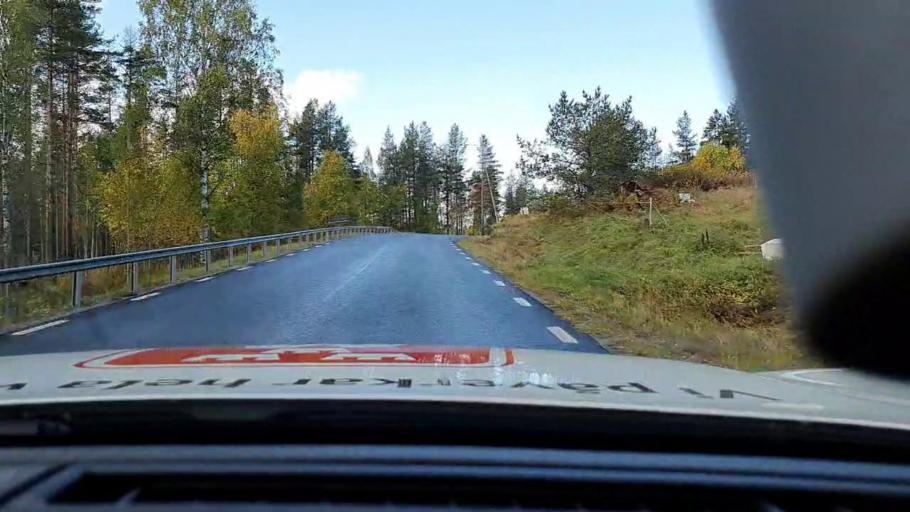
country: SE
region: Vaesterbotten
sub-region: Skelleftea Kommun
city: Langsele
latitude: 64.9462
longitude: 20.0253
